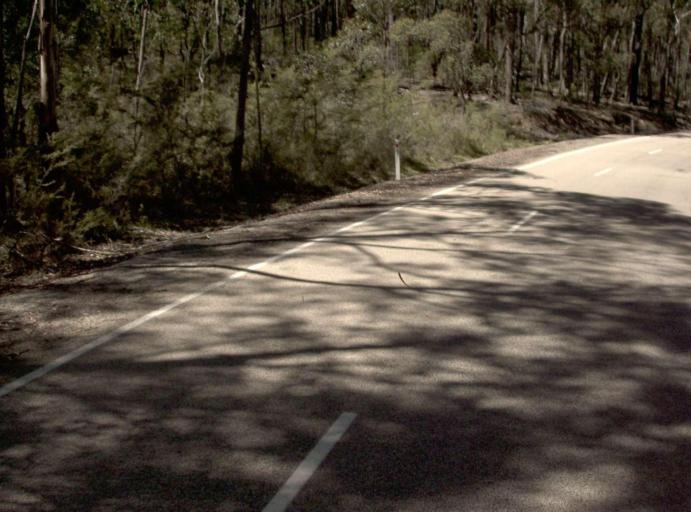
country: AU
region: Victoria
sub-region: East Gippsland
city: Lakes Entrance
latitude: -37.2916
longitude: 148.2560
